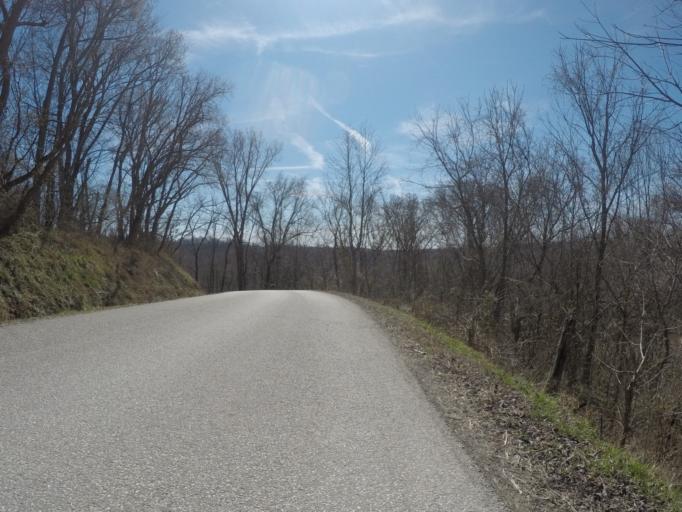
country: US
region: Ohio
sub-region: Lawrence County
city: South Point
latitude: 38.4814
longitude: -82.5669
